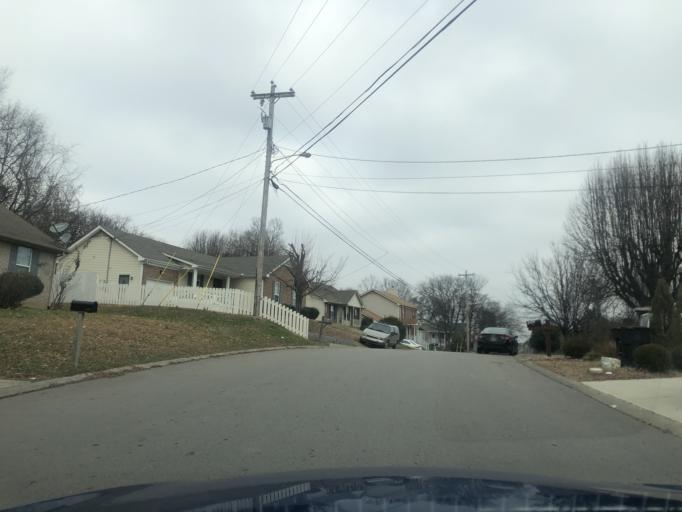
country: US
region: Tennessee
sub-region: Davidson County
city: Oak Hill
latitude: 36.0870
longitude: -86.7055
